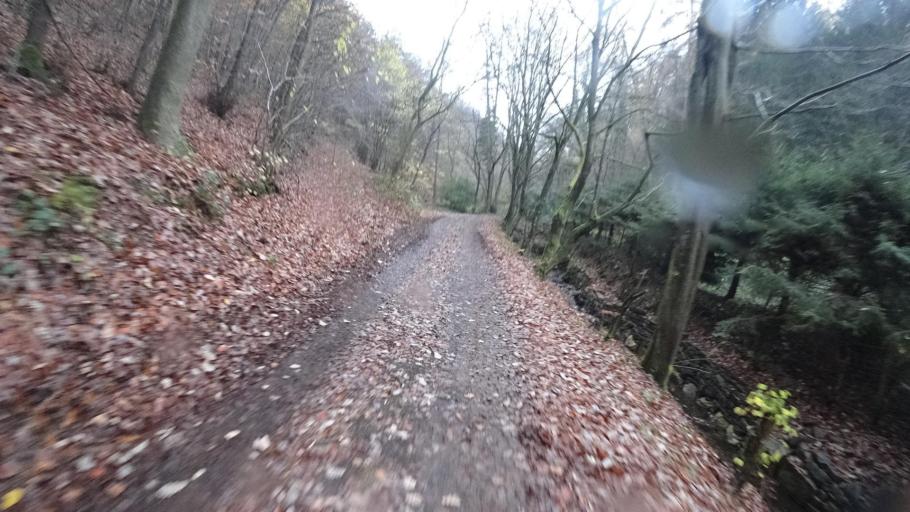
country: DE
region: Rheinland-Pfalz
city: Bad Neuenahr-Ahrweiler
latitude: 50.5185
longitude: 7.0938
